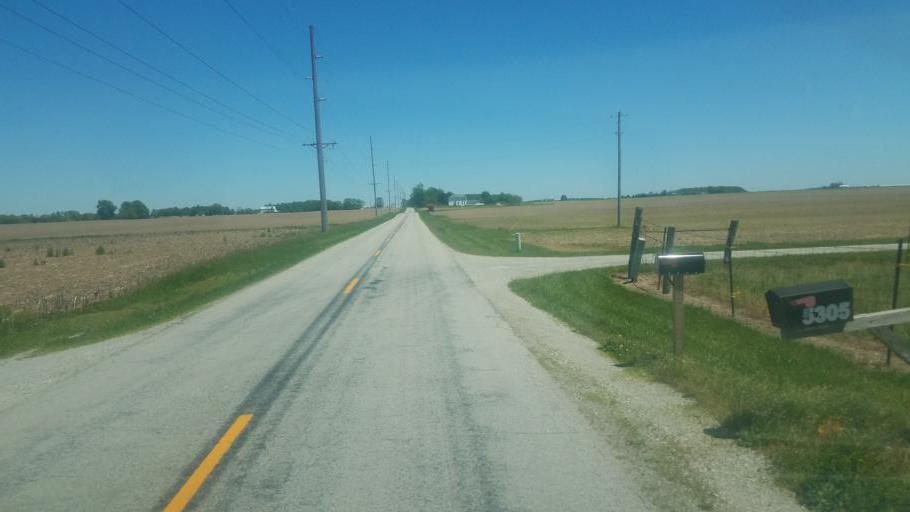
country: US
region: Ohio
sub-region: Miami County
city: Covington
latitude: 40.2272
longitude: -84.3322
